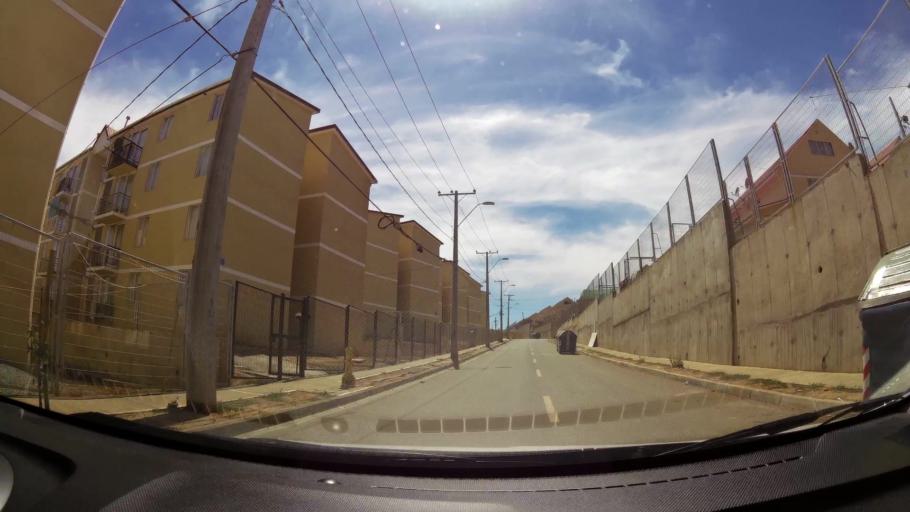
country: CL
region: Biobio
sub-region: Provincia de Concepcion
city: Talcahuano
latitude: -36.7112
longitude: -73.1335
